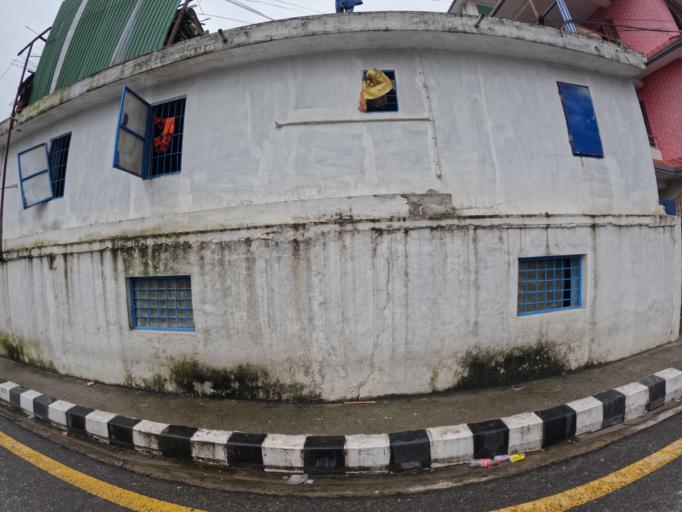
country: NP
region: Central Region
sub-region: Bagmati Zone
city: Kathmandu
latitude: 27.7538
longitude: 85.3257
